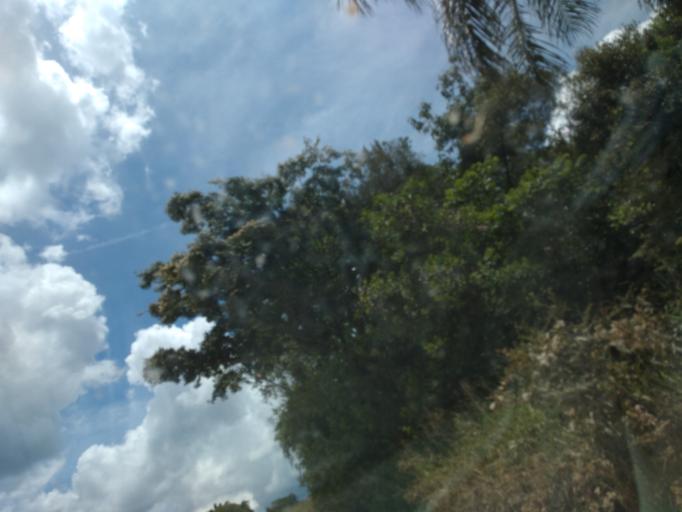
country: BR
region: Minas Gerais
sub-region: Sao Joao Del Rei
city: Sao Joao del Rei
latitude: -20.8882
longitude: -44.3093
